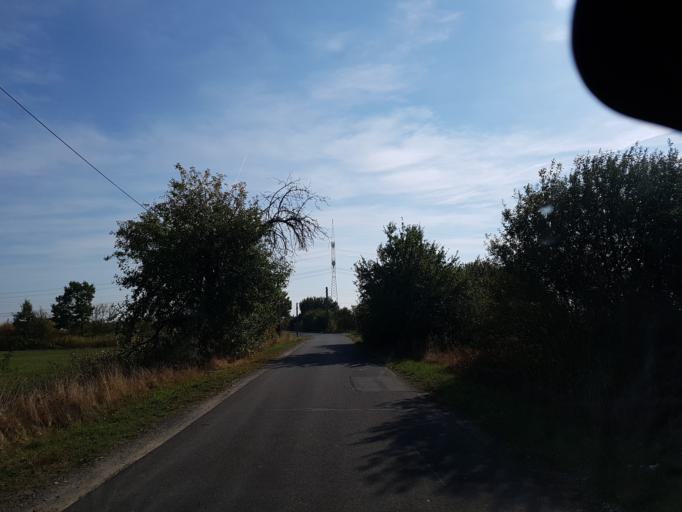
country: DE
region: Brandenburg
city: Doberlug-Kirchhain
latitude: 51.6453
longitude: 13.5461
